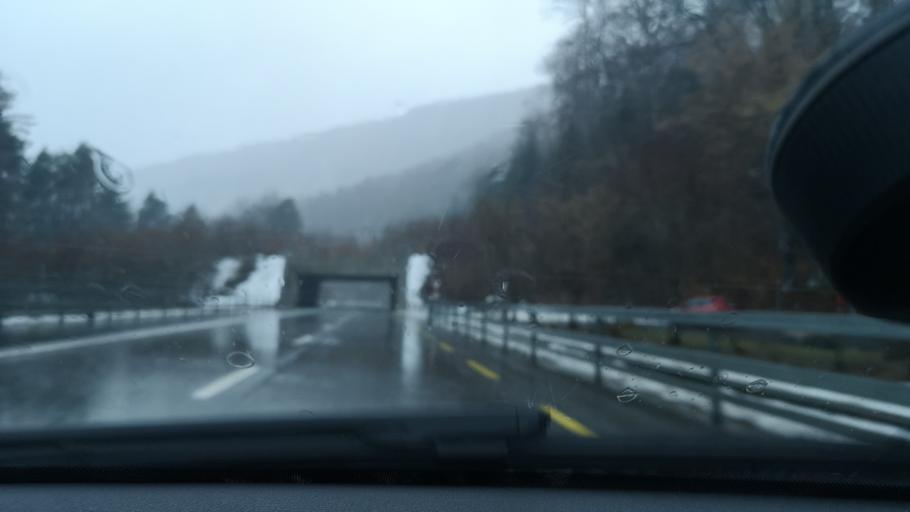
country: CH
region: Neuchatel
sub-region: Boudry District
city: Bevaix
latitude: 46.9679
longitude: 6.7881
